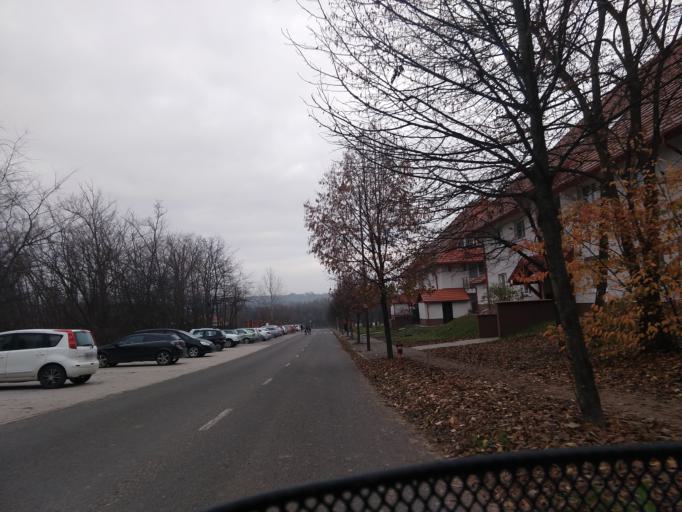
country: HU
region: Pest
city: Orbottyan
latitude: 47.6629
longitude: 19.2683
